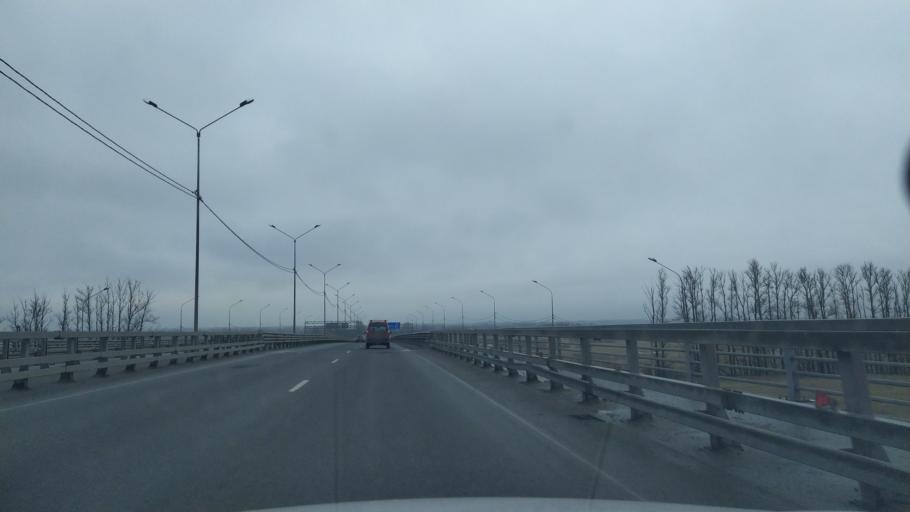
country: RU
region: St.-Petersburg
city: Aleksandrovskaya
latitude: 59.7180
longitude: 30.2832
